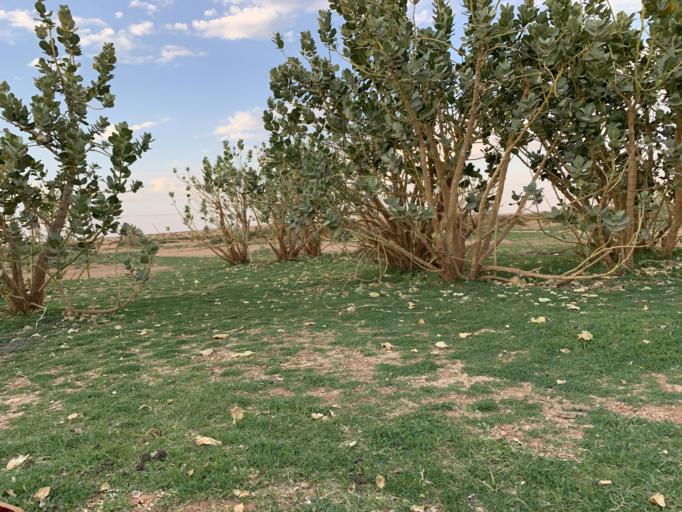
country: SA
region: Ar Riyad
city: Tumayr
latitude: 25.9000
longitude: 45.8276
